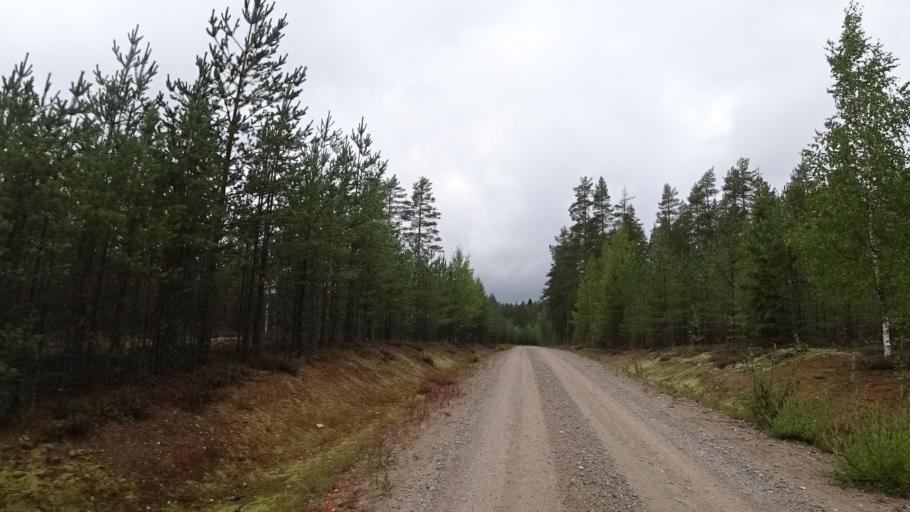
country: FI
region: North Karelia
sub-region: Pielisen Karjala
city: Lieksa
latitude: 63.5292
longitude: 30.0698
